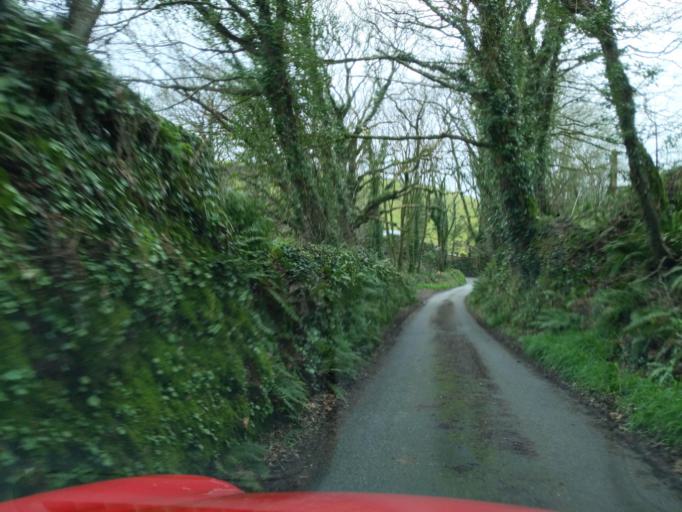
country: GB
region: England
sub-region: Cornwall
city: Duloe
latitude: 50.3510
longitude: -4.5129
